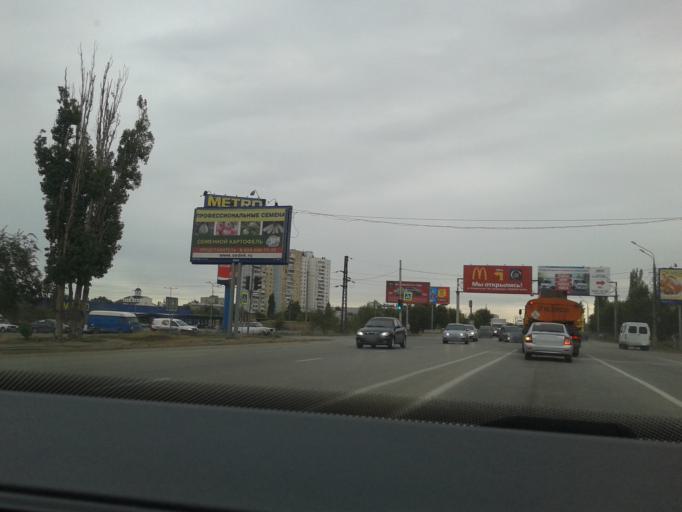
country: RU
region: Volgograd
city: Gorodishche
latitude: 48.7730
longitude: 44.4697
